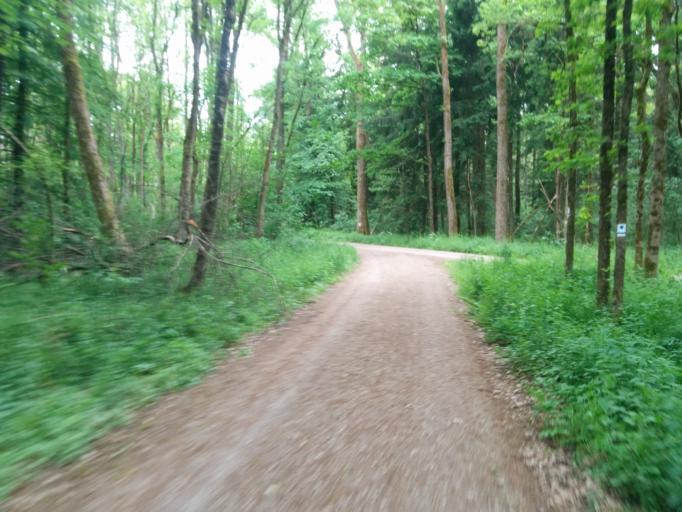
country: DE
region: Bavaria
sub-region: Regierungsbezirk Mittelfranken
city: Kalchreuth
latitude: 49.5213
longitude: 11.0893
